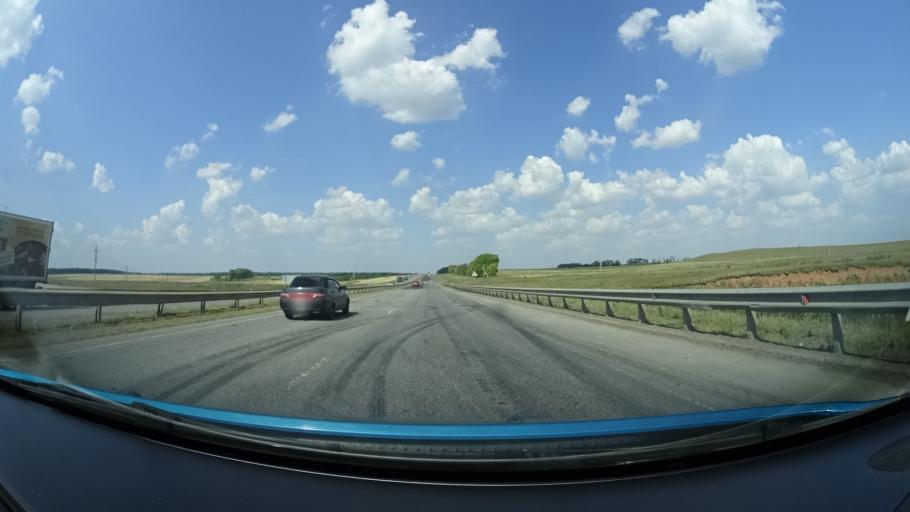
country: RU
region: Bashkortostan
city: Alekseyevka
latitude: 54.7274
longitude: 55.1520
